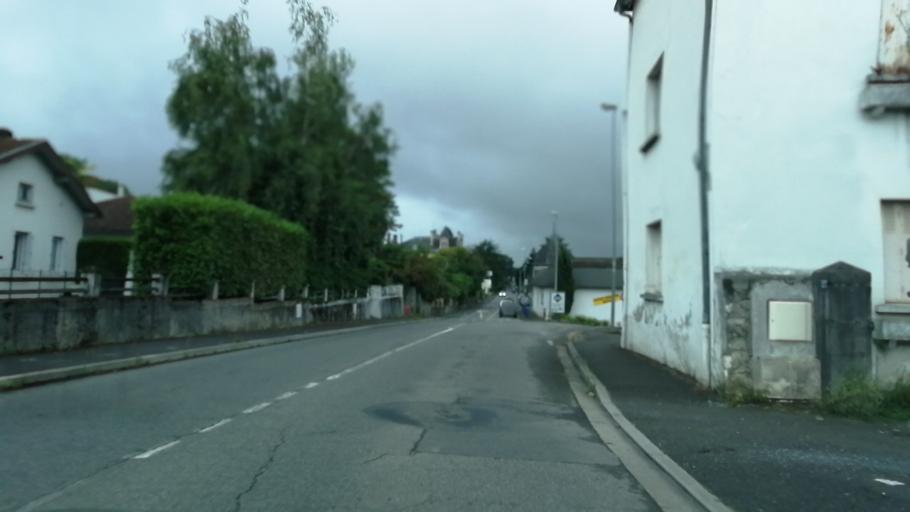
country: FR
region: Aquitaine
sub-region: Departement des Pyrenees-Atlantiques
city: Oloron-Sainte-Marie
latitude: 43.1791
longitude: -0.6066
